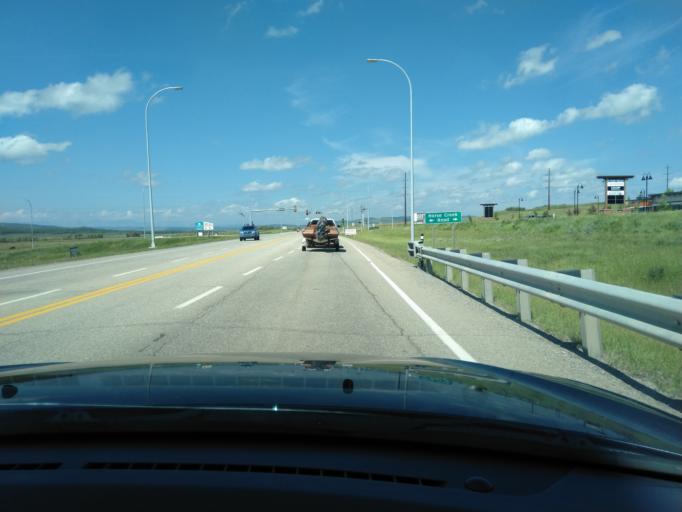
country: CA
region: Alberta
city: Cochrane
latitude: 51.2057
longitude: -114.5104
